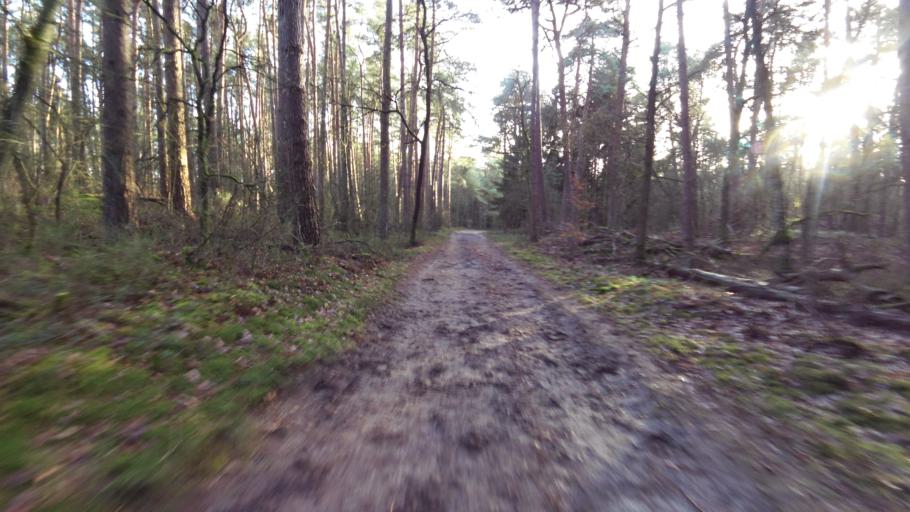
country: NL
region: Gelderland
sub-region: Gemeente Epe
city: Vaassen
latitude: 52.2624
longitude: 5.9191
